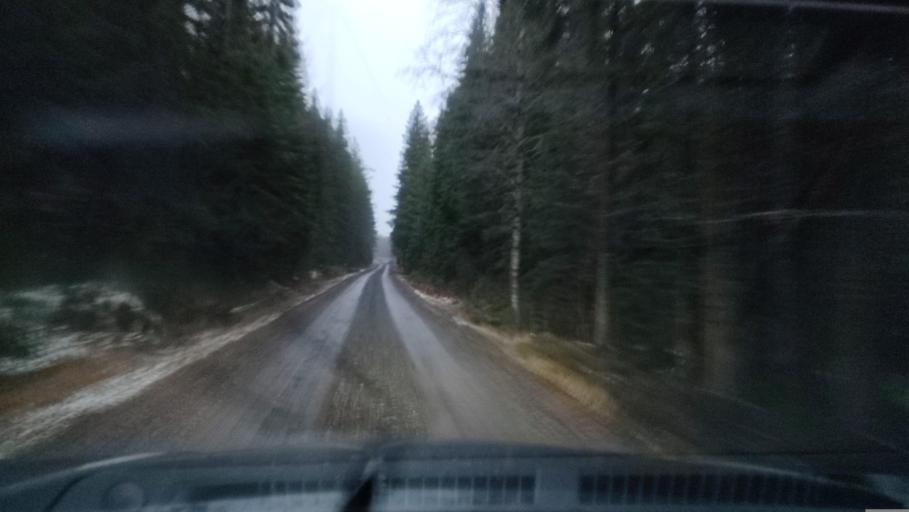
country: FI
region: Southern Ostrobothnia
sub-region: Suupohja
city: Karijoki
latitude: 62.1414
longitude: 21.6273
